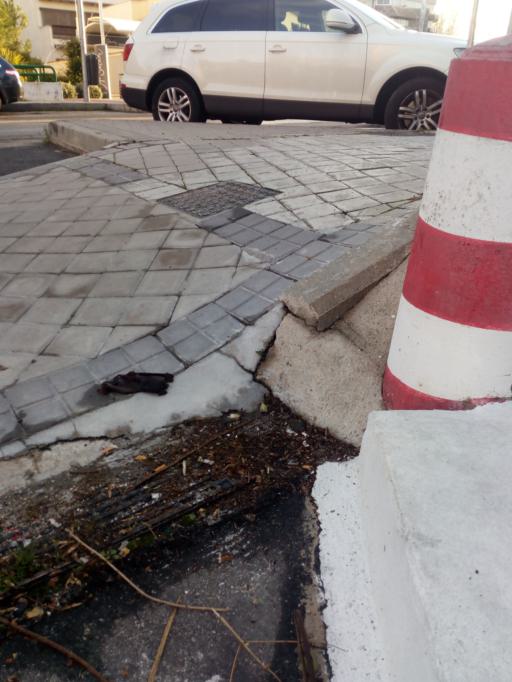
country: ES
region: Madrid
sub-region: Provincia de Madrid
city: Retiro
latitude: 40.4130
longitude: -3.6751
